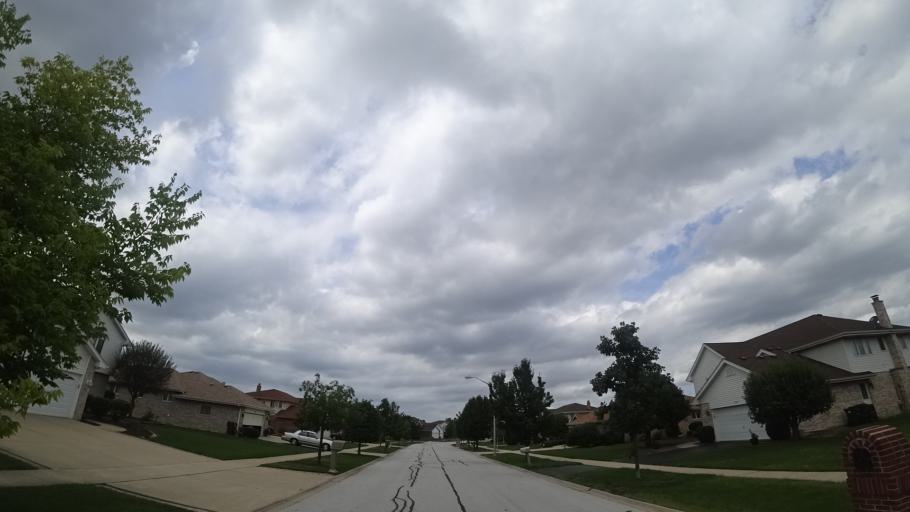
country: US
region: Illinois
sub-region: Cook County
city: Orland Hills
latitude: 41.5615
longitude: -87.8260
